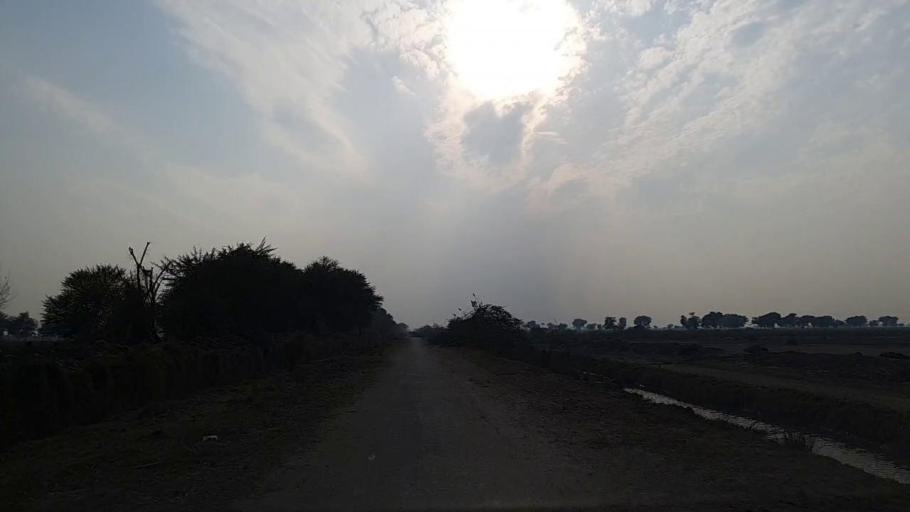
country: PK
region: Sindh
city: Jam Sahib
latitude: 26.3045
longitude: 68.5175
